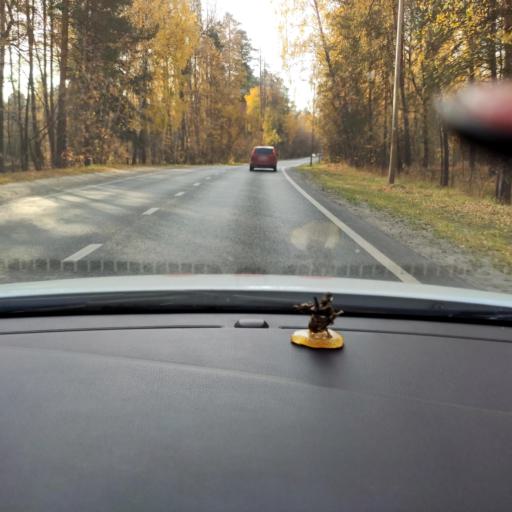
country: RU
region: Tatarstan
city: Osinovo
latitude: 55.8337
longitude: 48.8929
